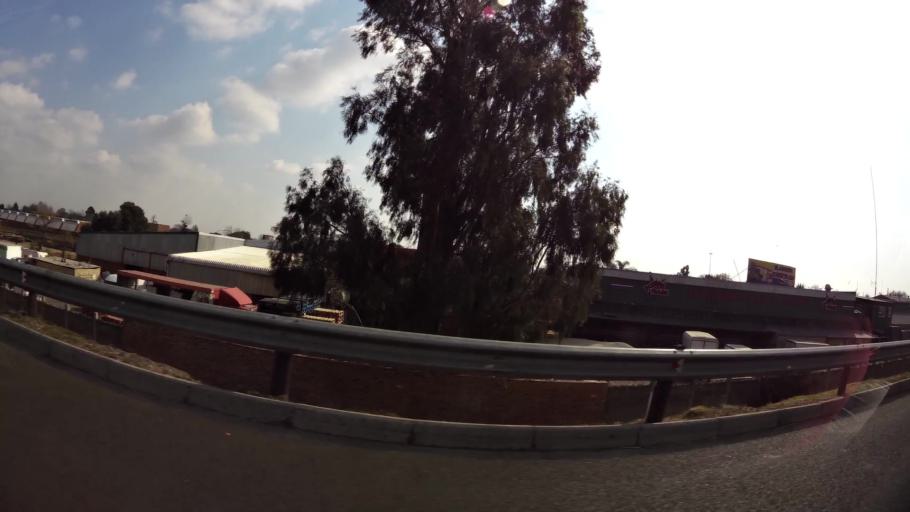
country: ZA
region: Gauteng
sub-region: Ekurhuleni Metropolitan Municipality
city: Brakpan
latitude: -26.1591
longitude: 28.4187
